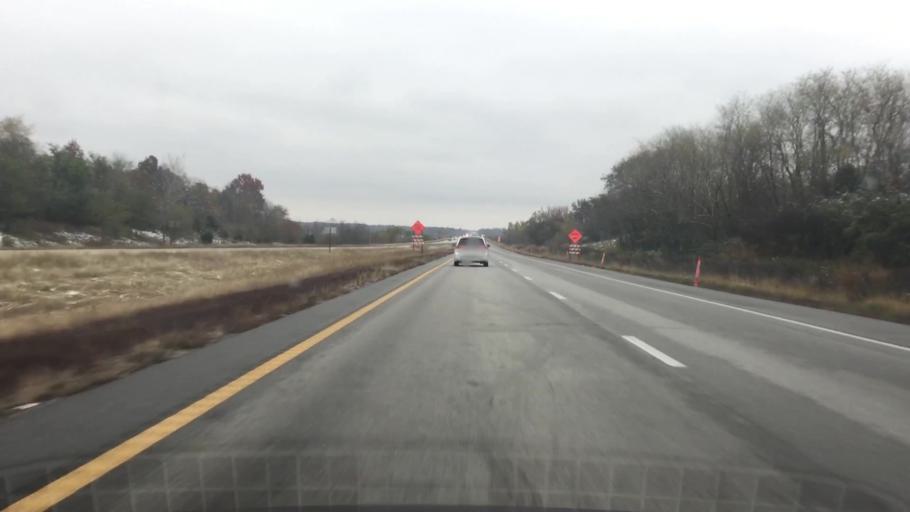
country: US
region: Missouri
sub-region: Henry County
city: Clinton
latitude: 38.2960
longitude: -93.7591
